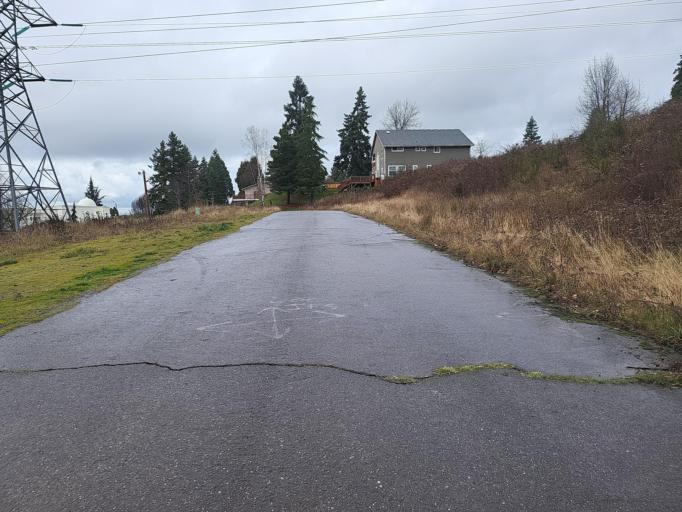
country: US
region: Washington
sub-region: King County
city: Renton
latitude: 47.4698
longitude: -122.1989
